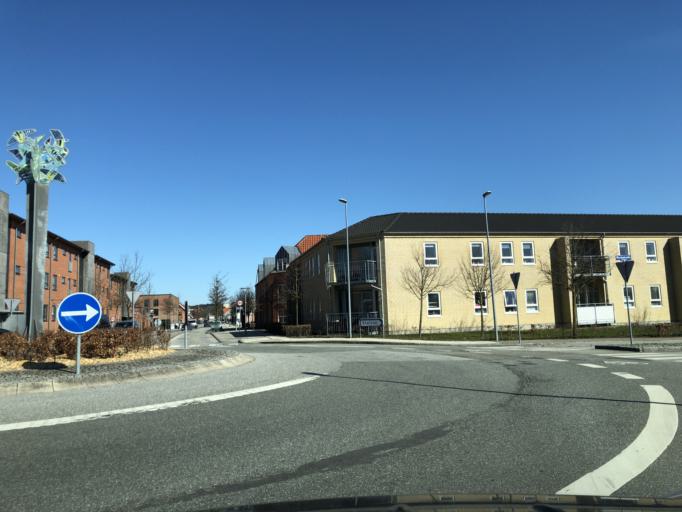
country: DK
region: North Denmark
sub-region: Rebild Kommune
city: Stovring
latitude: 56.8874
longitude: 9.8373
